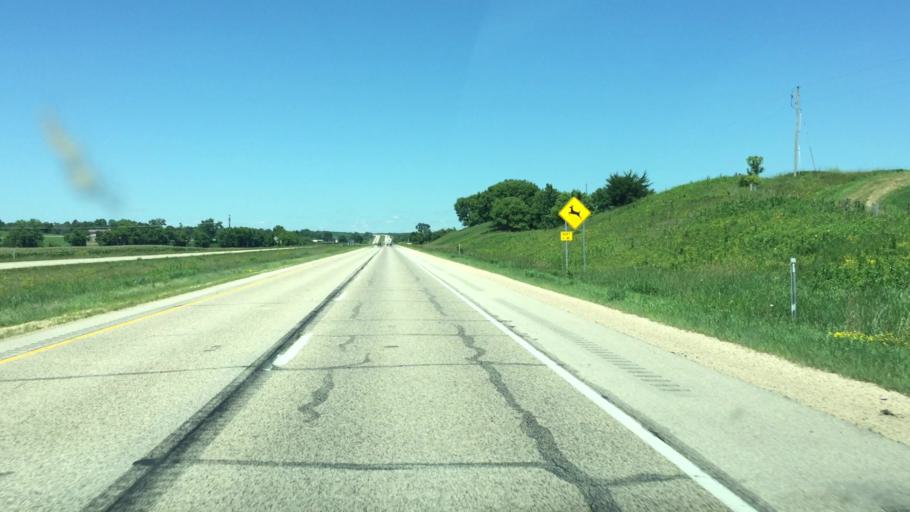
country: US
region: Iowa
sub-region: Jackson County
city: Maquoketa
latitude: 42.1668
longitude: -90.6751
